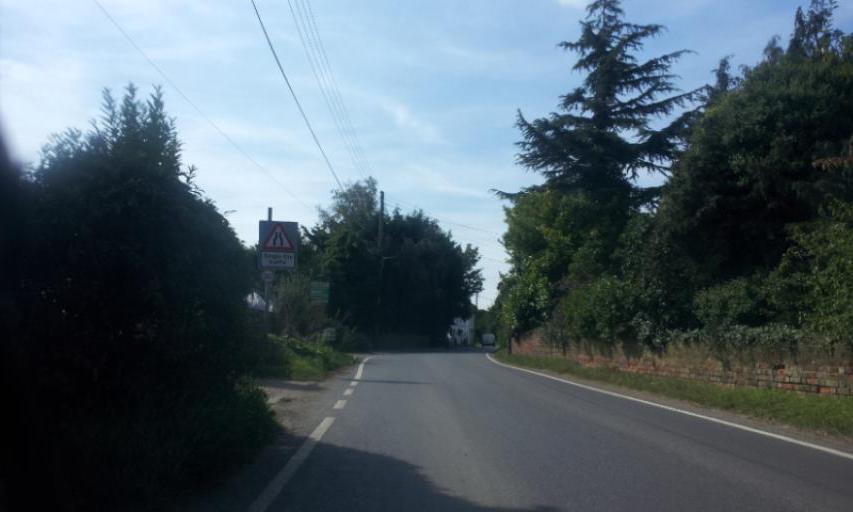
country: GB
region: England
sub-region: Kent
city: Newington
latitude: 51.3274
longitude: 0.6839
